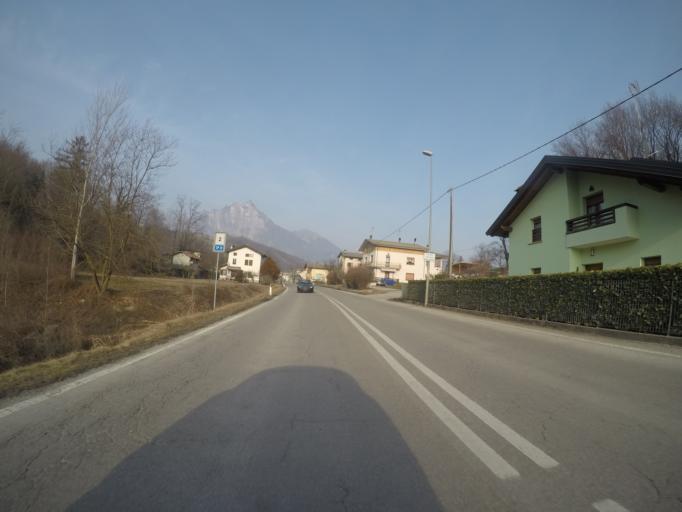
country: IT
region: Veneto
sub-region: Provincia di Belluno
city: Sospirolo
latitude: 46.1452
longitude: 12.1048
